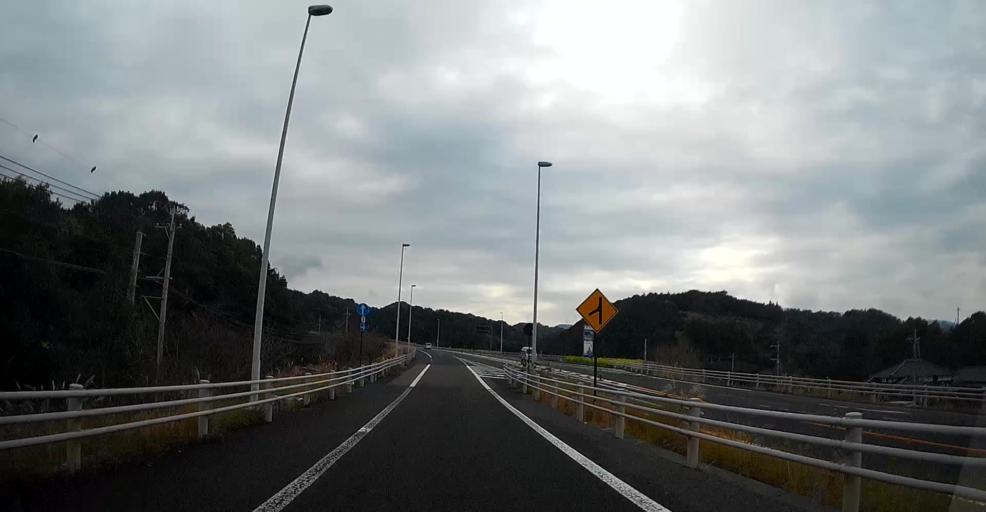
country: JP
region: Kumamoto
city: Hondo
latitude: 32.5030
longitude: 130.3040
